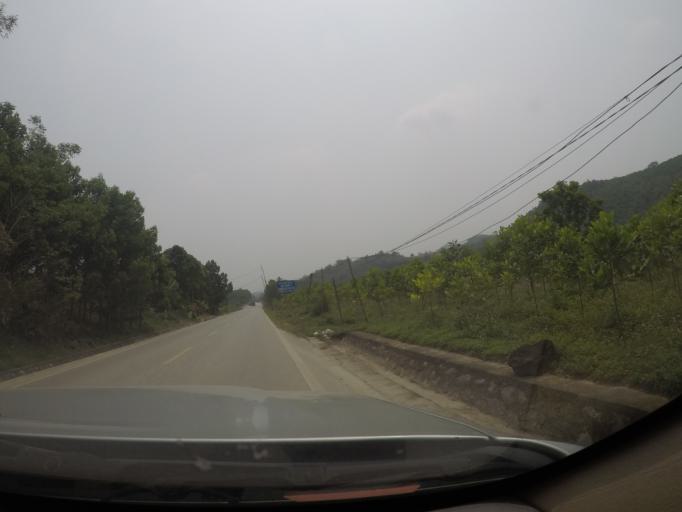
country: VN
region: Thanh Hoa
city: Thi Tran Yen Cat
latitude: 19.7530
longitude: 105.4215
